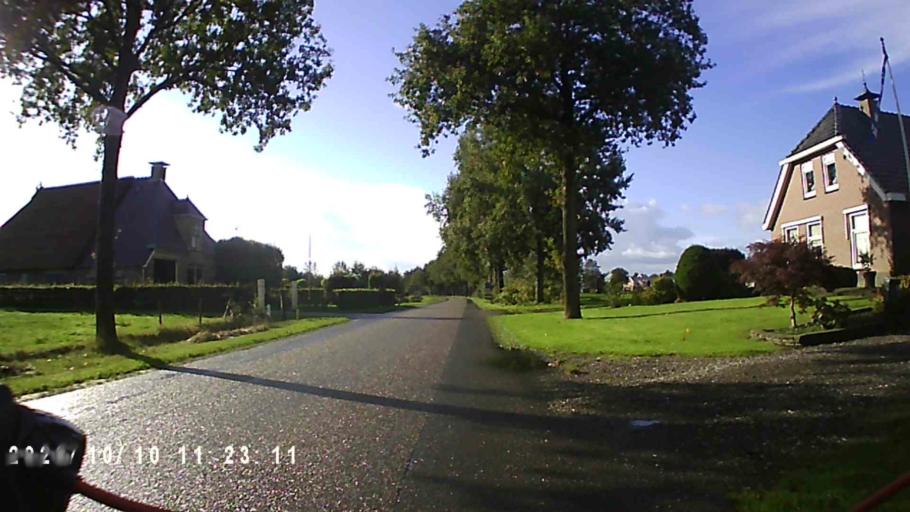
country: NL
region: Friesland
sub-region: Gemeente Smallingerland
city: Drachtstercompagnie
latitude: 53.0909
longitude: 6.1771
